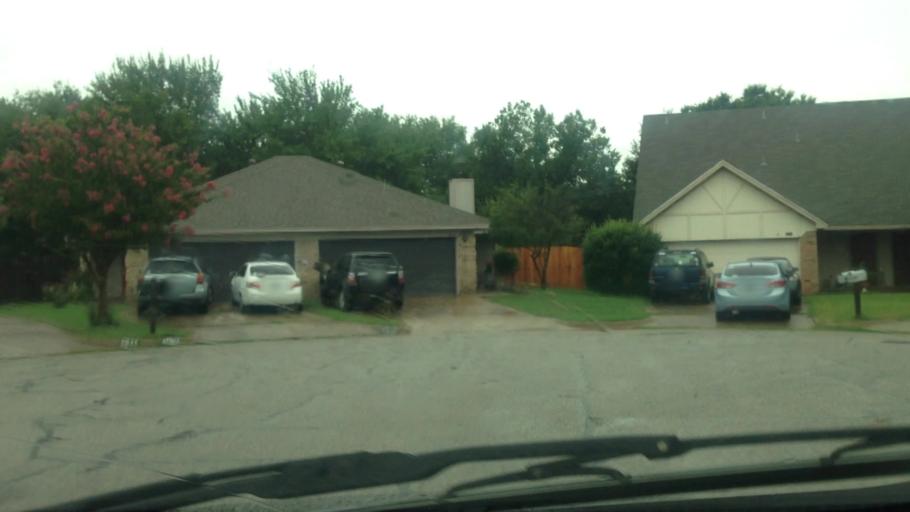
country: US
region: Texas
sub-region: Tarrant County
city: North Richland Hills
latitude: 32.8633
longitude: -97.2179
